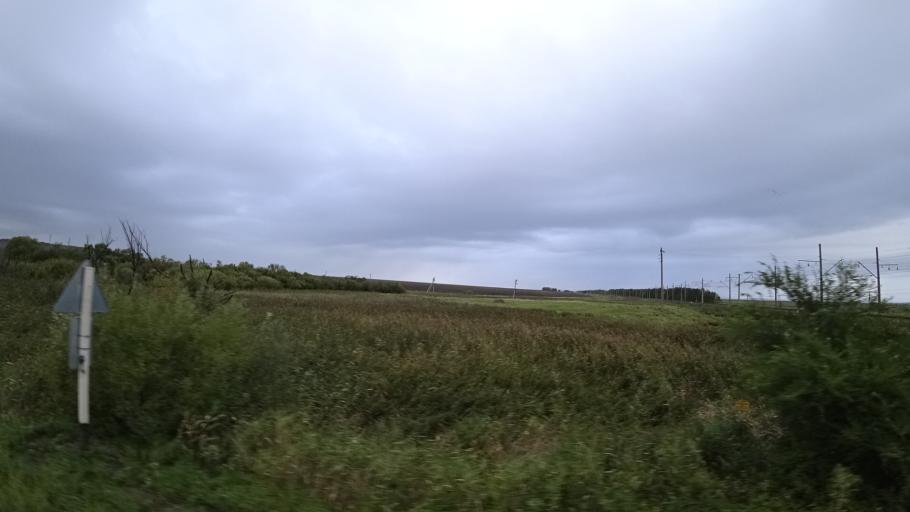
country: RU
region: Primorskiy
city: Chernigovka
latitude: 44.3637
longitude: 132.5502
